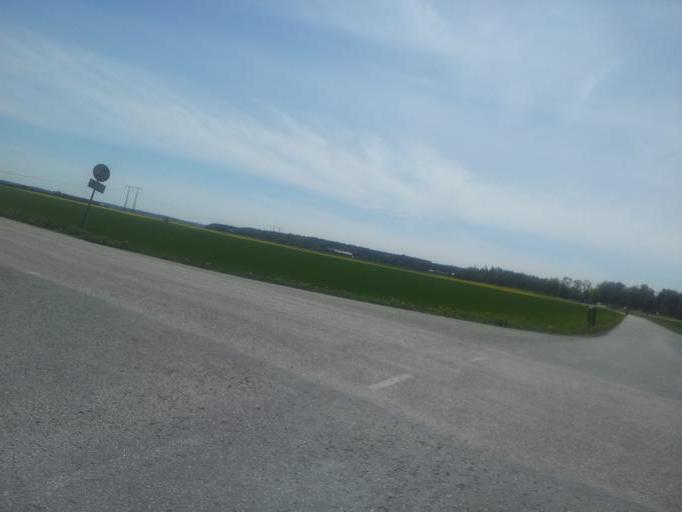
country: SE
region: Uppsala
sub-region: Uppsala Kommun
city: Saevja
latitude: 59.8479
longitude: 17.7390
